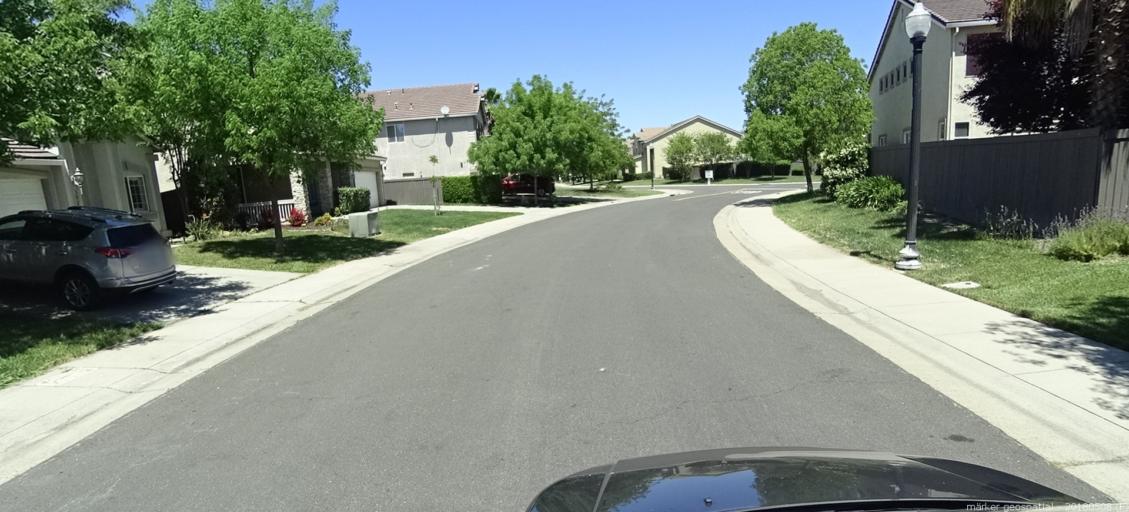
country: US
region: California
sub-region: Sacramento County
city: Elverta
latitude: 38.6768
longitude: -121.5272
